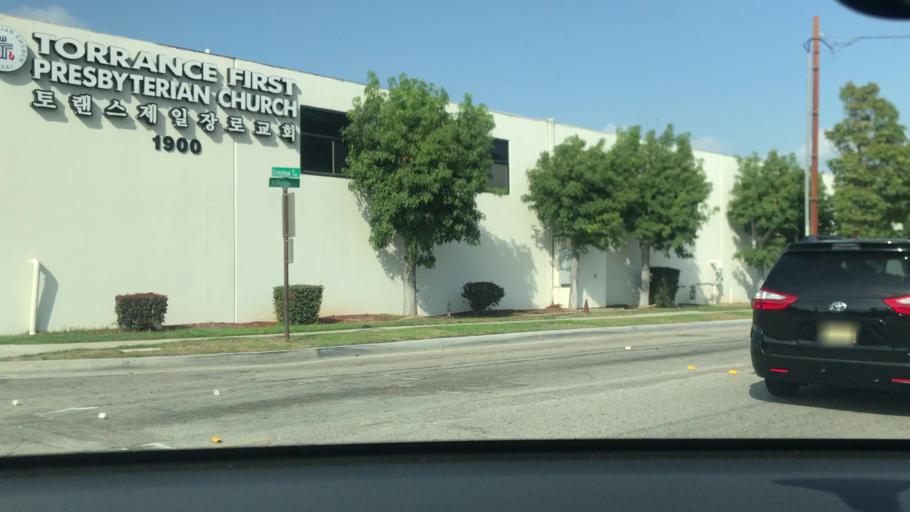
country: US
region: California
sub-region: Los Angeles County
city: Torrance
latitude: 33.8276
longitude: -118.3285
